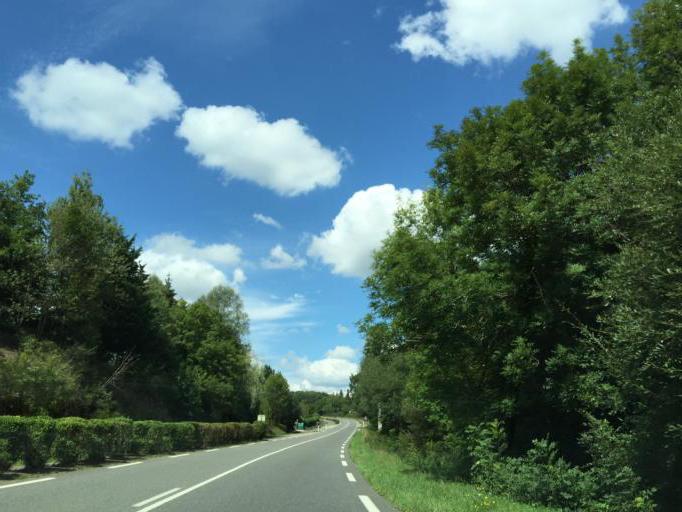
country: FR
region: Midi-Pyrenees
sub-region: Departement de l'Aveyron
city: Rodez
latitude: 44.3879
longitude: 2.5664
